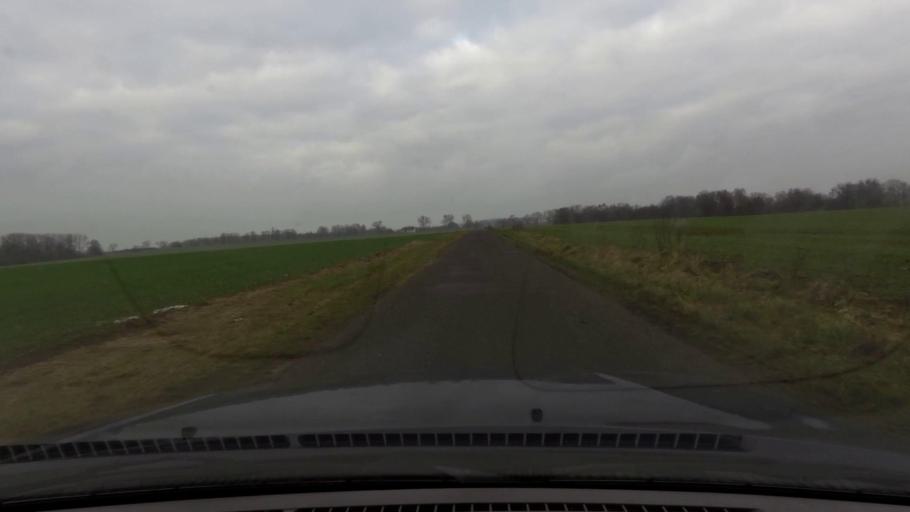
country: PL
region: West Pomeranian Voivodeship
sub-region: Powiat stargardzki
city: Stargard Szczecinski
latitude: 53.3417
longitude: 15.1263
